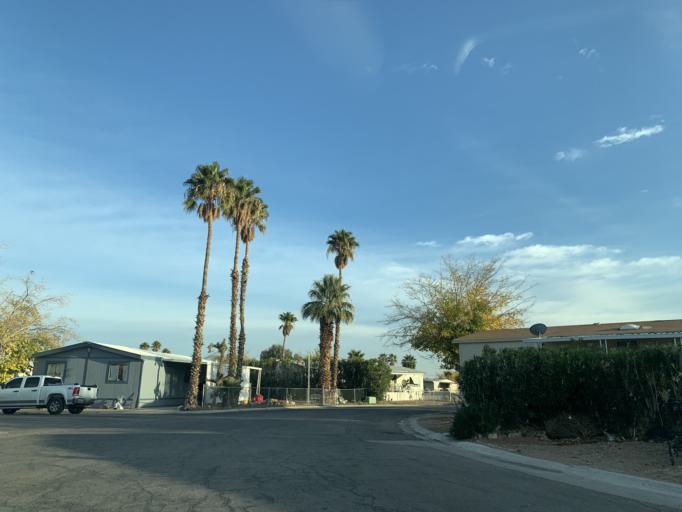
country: US
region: Nevada
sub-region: Clark County
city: Spring Valley
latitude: 36.1022
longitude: -115.2201
